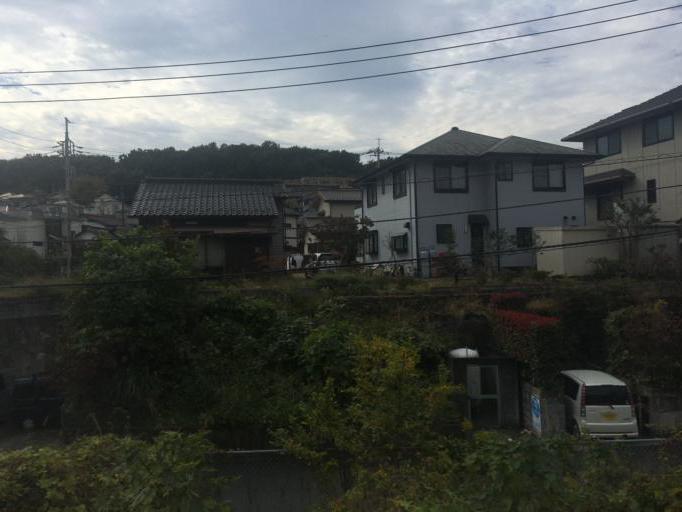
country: JP
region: Tokyo
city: Hino
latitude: 35.6884
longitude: 139.3656
